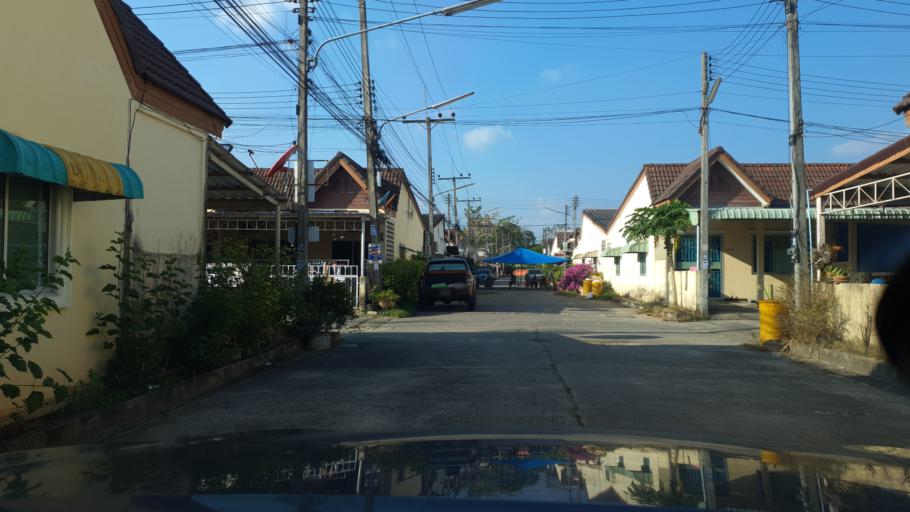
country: TH
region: Krabi
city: Nuea Khlong
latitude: 8.0821
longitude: 98.9891
